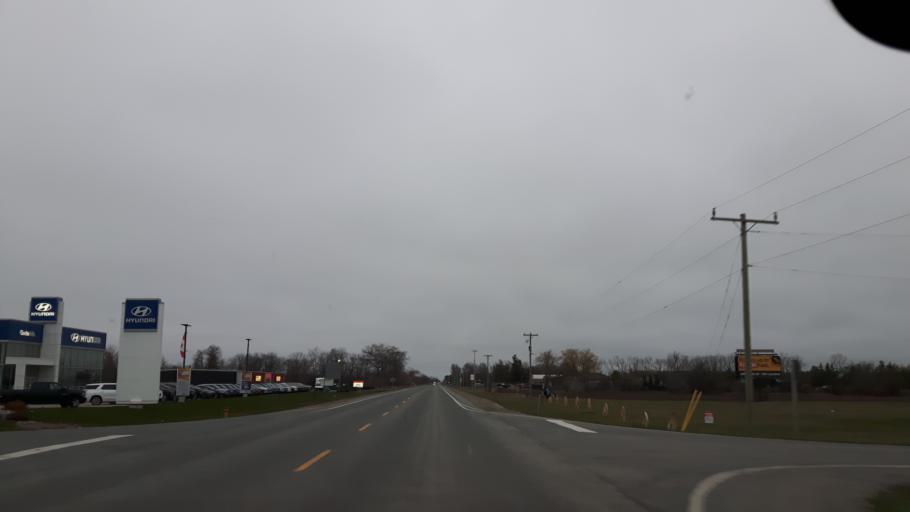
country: CA
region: Ontario
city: Goderich
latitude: 43.7228
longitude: -81.7058
